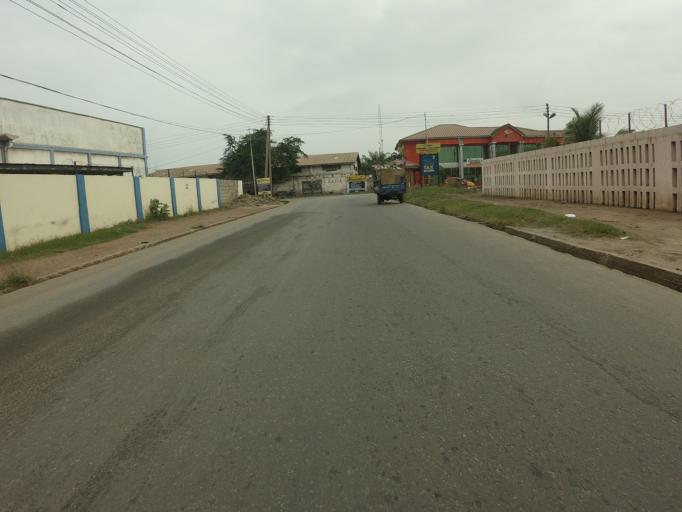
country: GH
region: Greater Accra
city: Accra
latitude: 5.5554
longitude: -0.2236
